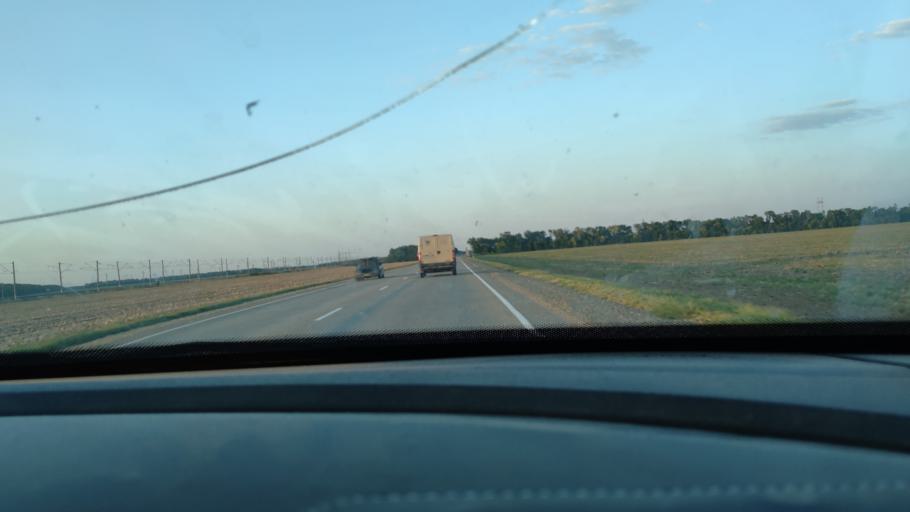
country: RU
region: Krasnodarskiy
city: Novominskaya
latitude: 46.3891
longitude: 38.9886
